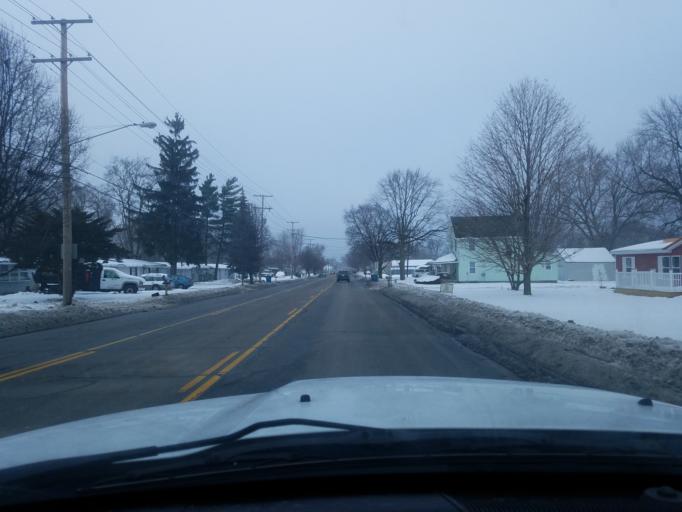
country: US
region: Indiana
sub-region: Saint Joseph County
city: Mishawaka
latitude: 41.6457
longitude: -86.1768
